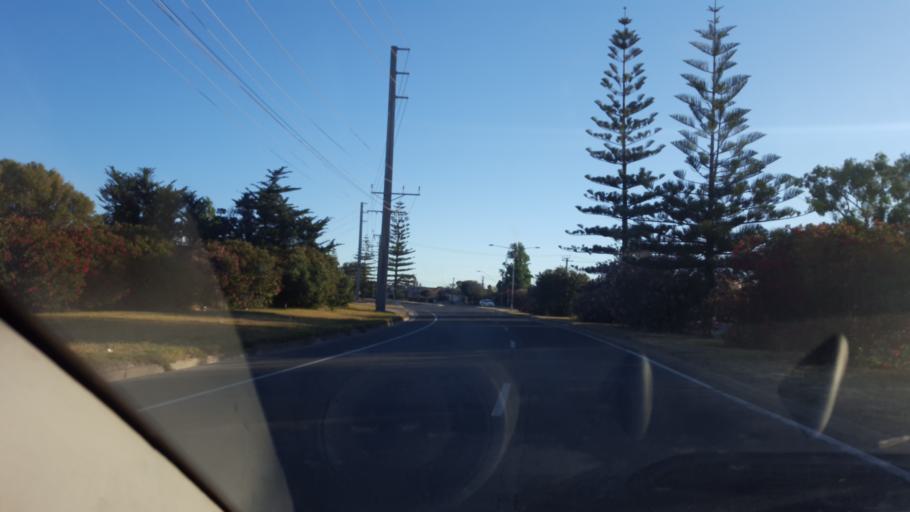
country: AU
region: South Australia
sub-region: Port Adelaide Enfield
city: Birkenhead
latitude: -34.8222
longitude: 138.5000
